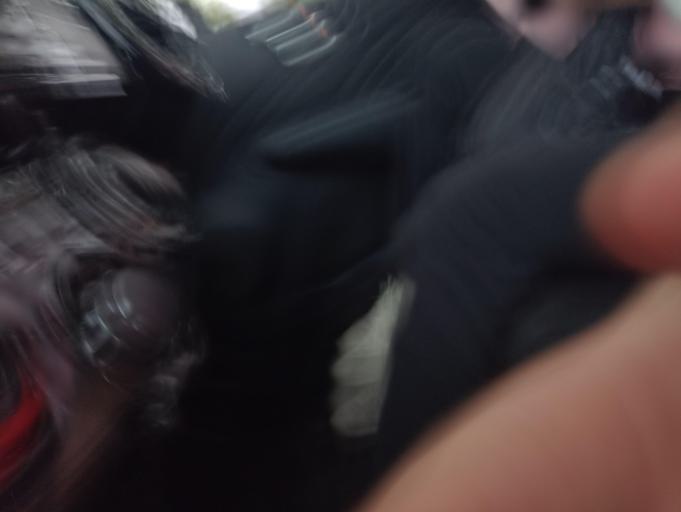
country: AR
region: Buenos Aires
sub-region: Partido de La Plata
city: La Plata
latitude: -34.8668
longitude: -58.0767
